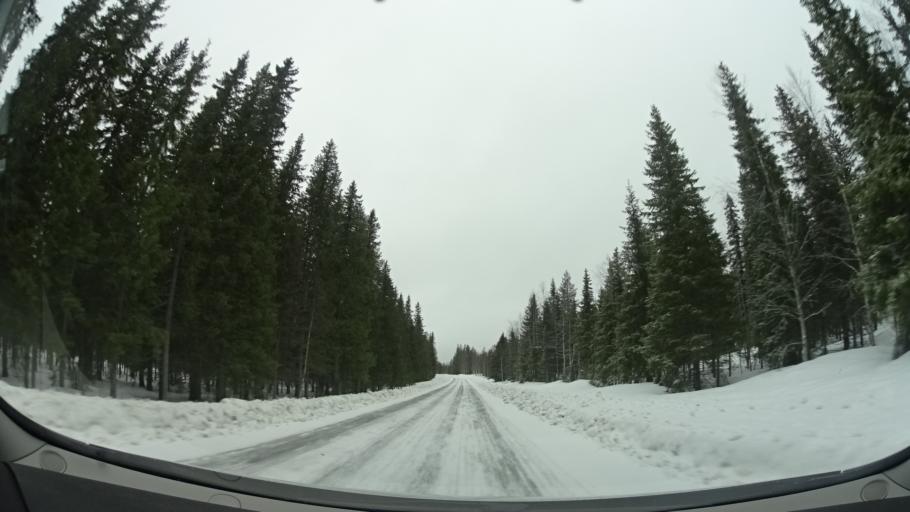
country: SE
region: Vaesterbotten
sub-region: Mala Kommun
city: Mala
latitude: 65.0971
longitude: 18.9212
